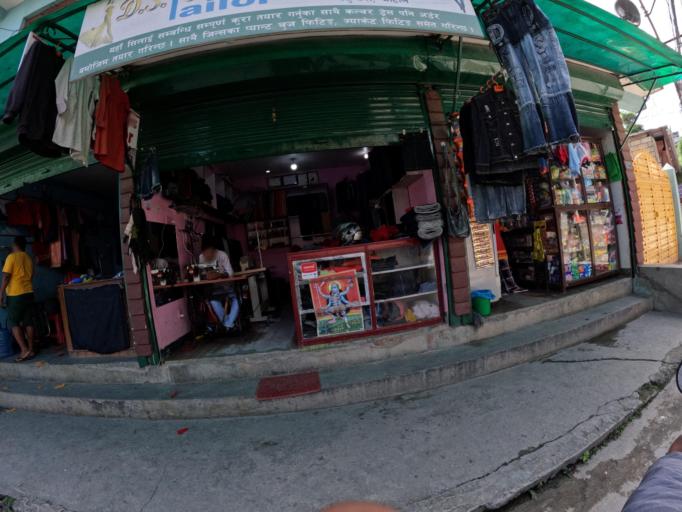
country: NP
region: Central Region
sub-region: Bagmati Zone
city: Kathmandu
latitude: 27.7441
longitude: 85.3320
